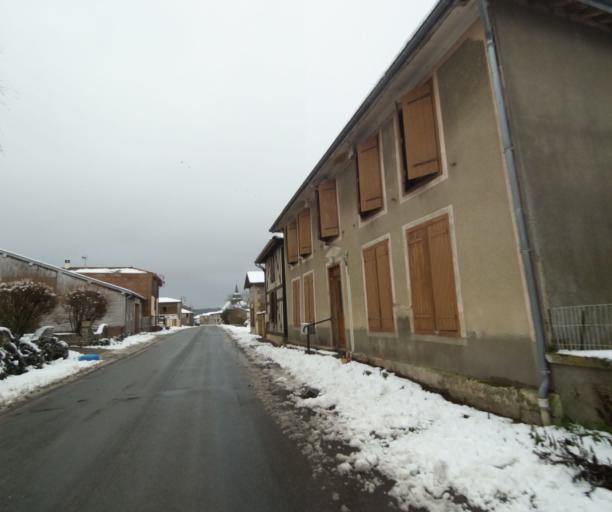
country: FR
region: Champagne-Ardenne
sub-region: Departement de la Haute-Marne
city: Laneuville-a-Remy
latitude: 48.4628
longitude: 4.8440
